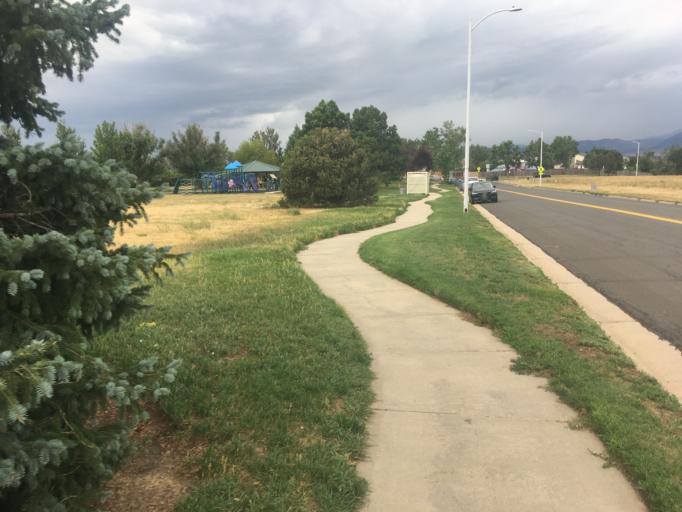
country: US
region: Colorado
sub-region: Broomfield County
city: Broomfield
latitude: 39.9343
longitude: -105.0979
